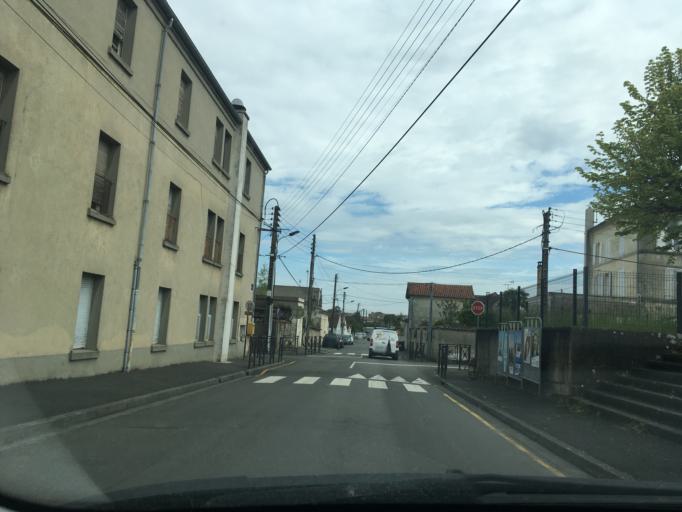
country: FR
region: Poitou-Charentes
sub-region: Departement de la Charente
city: Cognac
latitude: 45.6838
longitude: -0.3331
